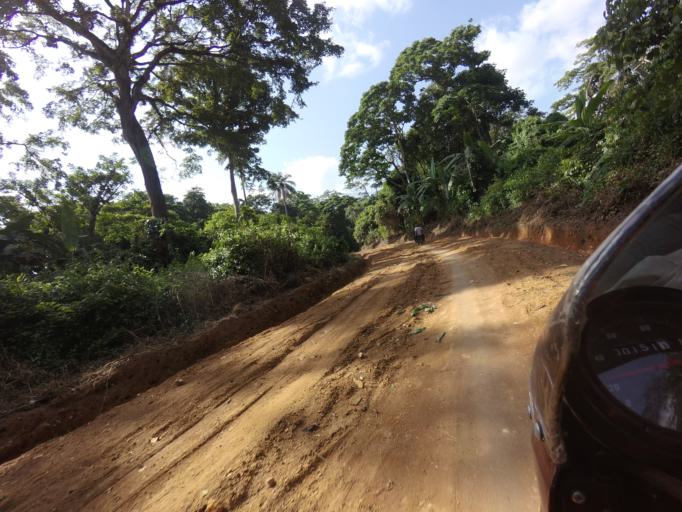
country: SL
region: Eastern Province
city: Kailahun
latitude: 8.3726
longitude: -10.7104
